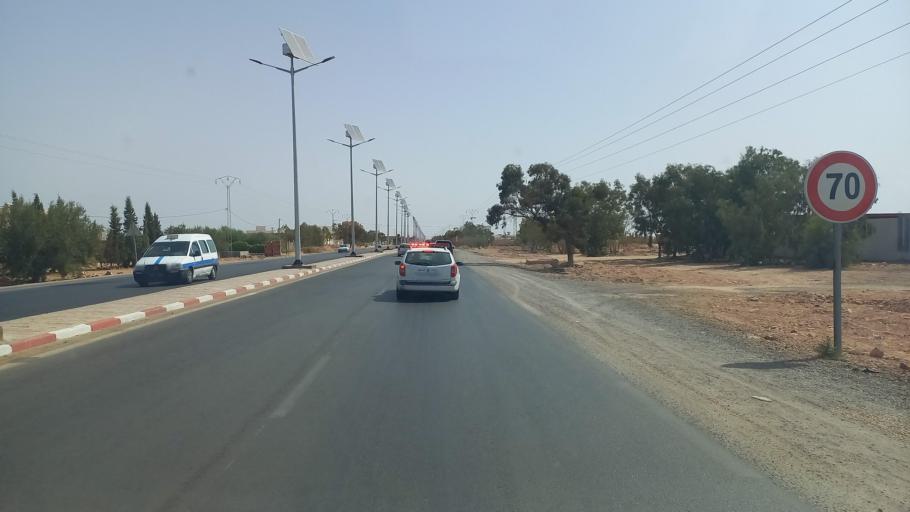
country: TN
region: Madanin
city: Medenine
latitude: 33.3529
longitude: 10.5358
